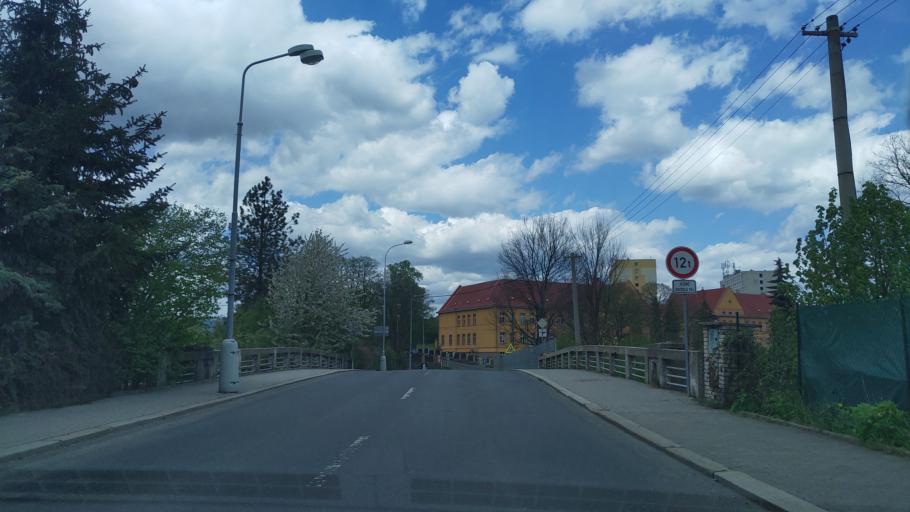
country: CZ
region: Ustecky
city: Trmice
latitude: 50.6433
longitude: 14.0040
